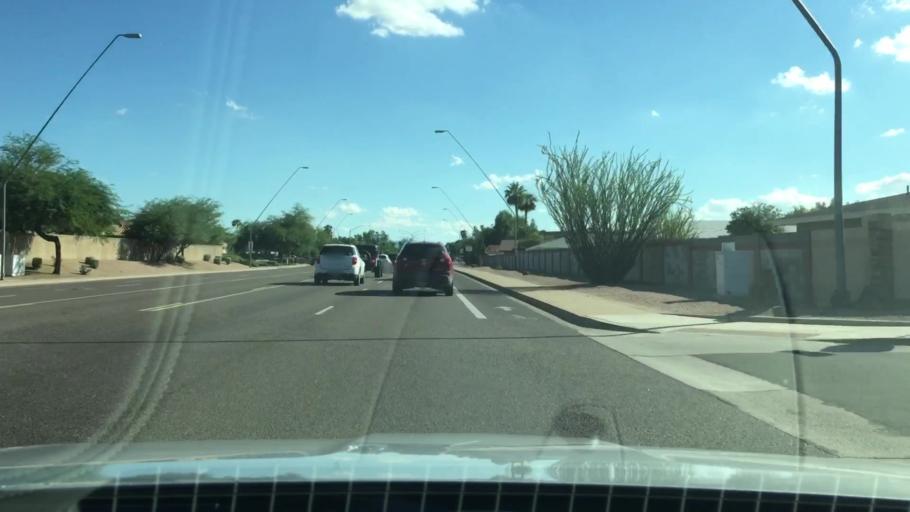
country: US
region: Arizona
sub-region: Maricopa County
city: Gilbert
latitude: 33.3969
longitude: -111.7194
